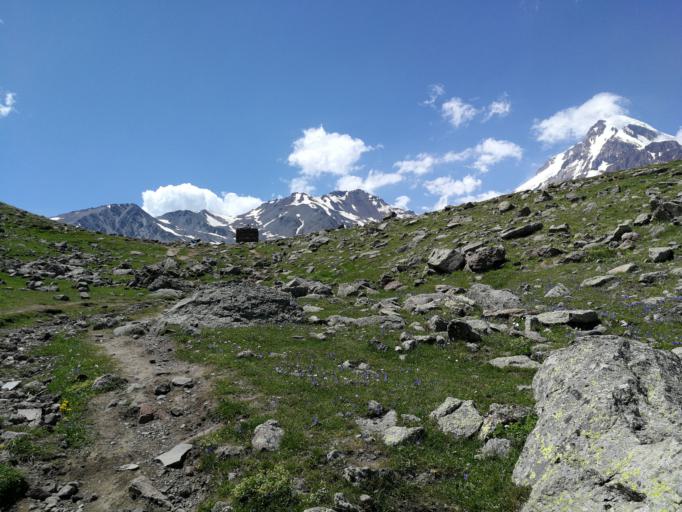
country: GE
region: Mtskheta-Mtianeti
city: Step'antsminda
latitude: 42.6588
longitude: 44.5742
